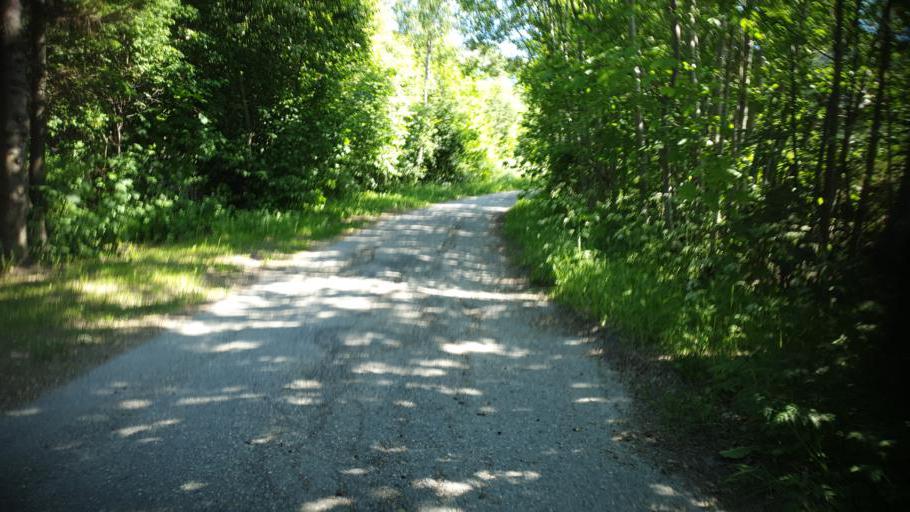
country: NO
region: Sor-Trondelag
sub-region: Malvik
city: Malvik
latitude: 63.4318
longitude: 10.5812
